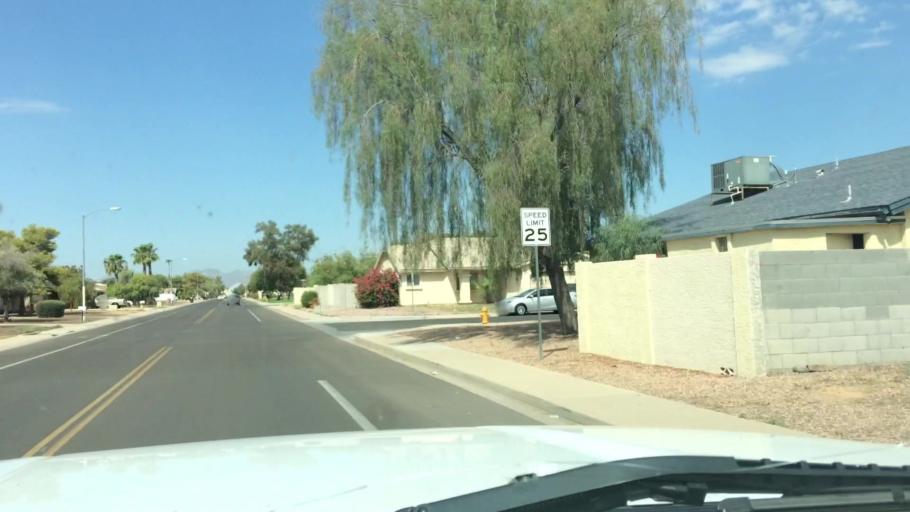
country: US
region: Arizona
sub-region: Maricopa County
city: Peoria
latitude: 33.5773
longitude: -112.2468
